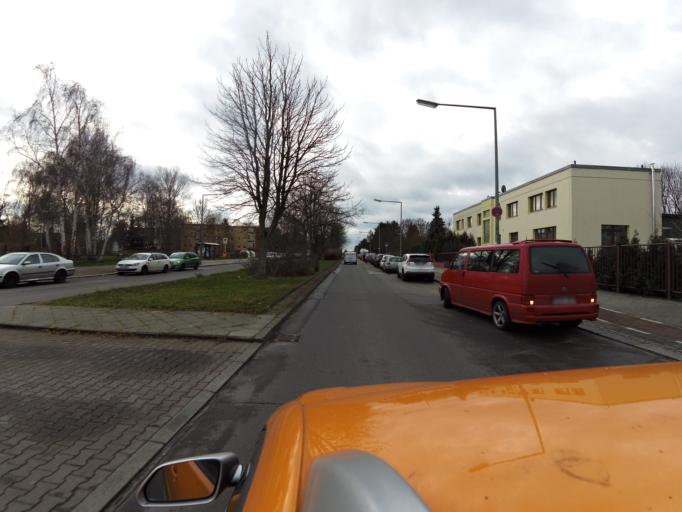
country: DE
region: Berlin
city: Rudow
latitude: 52.4192
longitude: 13.4792
